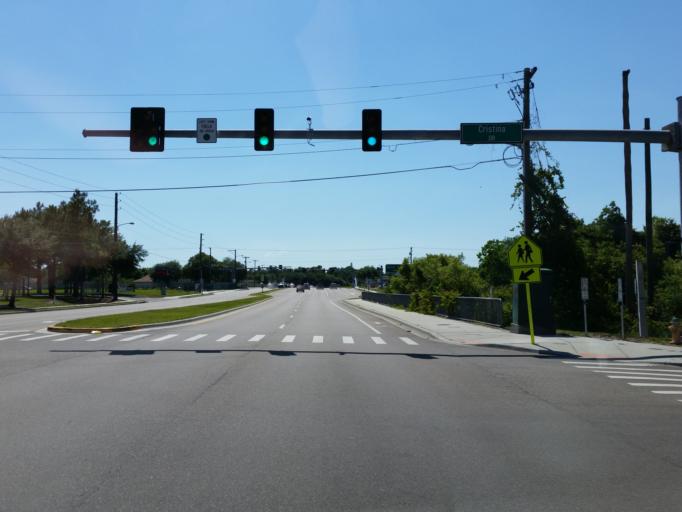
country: US
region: Florida
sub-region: Hillsborough County
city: Riverview
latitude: 27.8537
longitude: -82.3120
